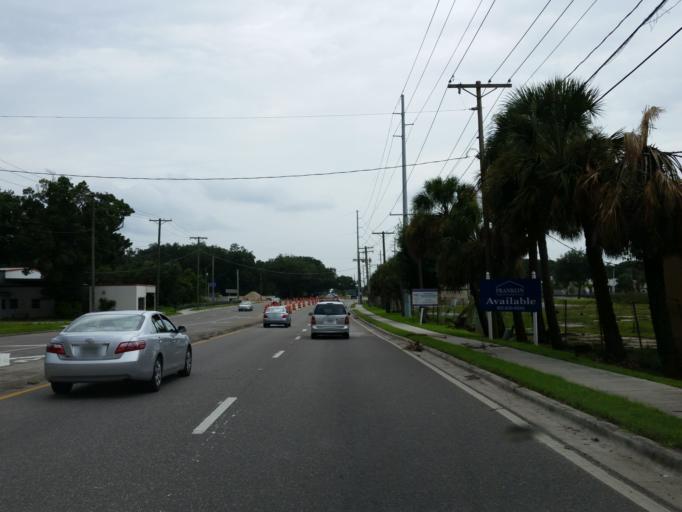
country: US
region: Florida
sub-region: Hillsborough County
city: Mango
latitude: 27.9719
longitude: -82.3352
